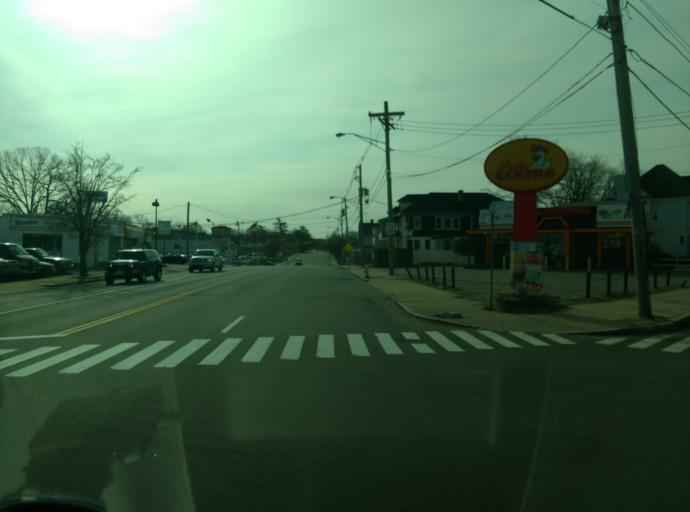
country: US
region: Massachusetts
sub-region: Essex County
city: Lawrence
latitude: 42.6923
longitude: -71.1533
